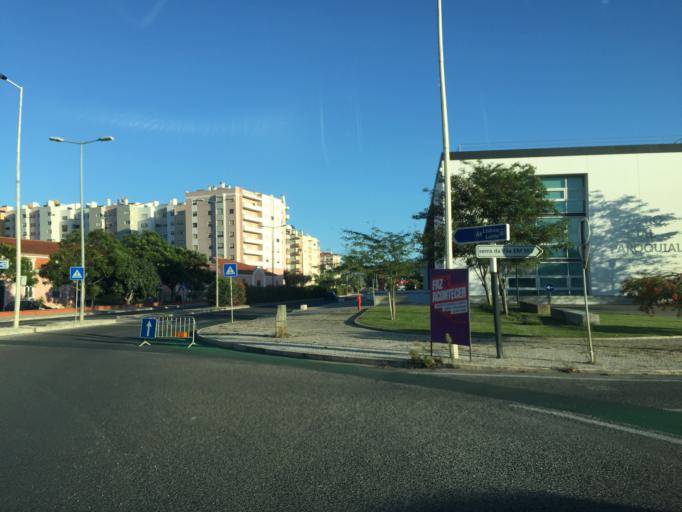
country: PT
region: Lisbon
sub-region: Torres Vedras
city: Torres Vedras
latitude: 39.0841
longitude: -9.2613
